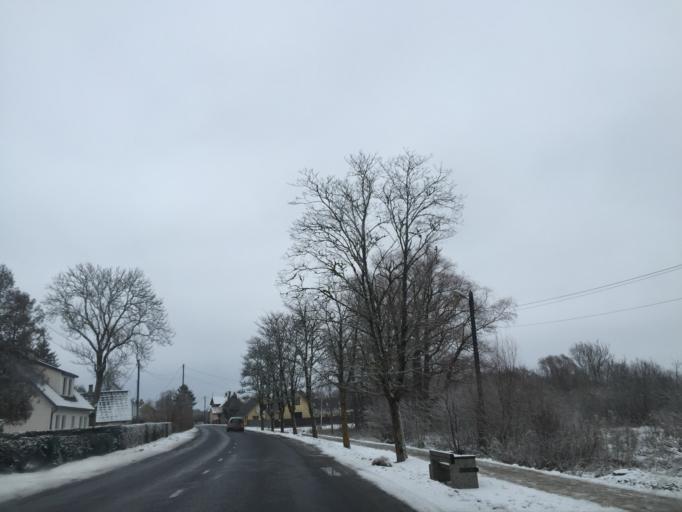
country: EE
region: Laeaene
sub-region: Lihula vald
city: Lihula
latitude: 58.6828
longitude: 23.8256
